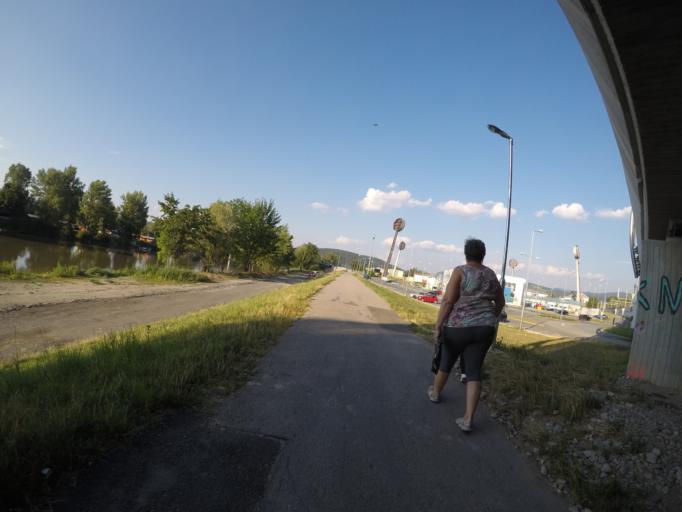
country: SK
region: Trenciansky
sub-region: Okres Trencin
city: Trencin
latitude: 48.8982
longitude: 18.0407
